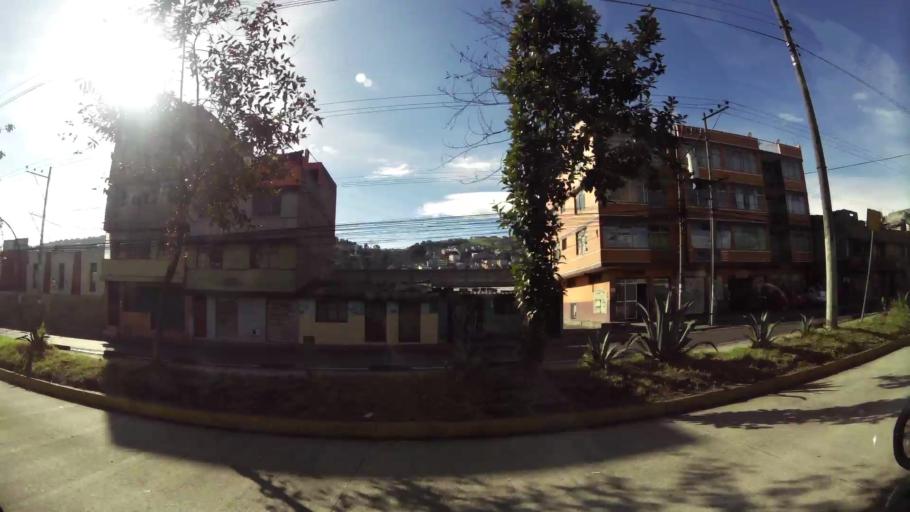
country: EC
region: Pichincha
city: Quito
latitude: -0.2917
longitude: -78.5393
